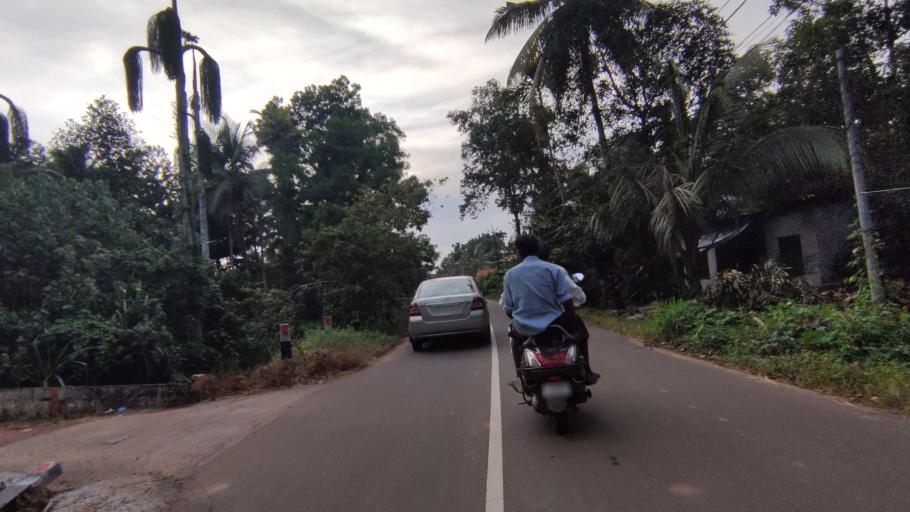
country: IN
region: Kerala
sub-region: Kottayam
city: Kottayam
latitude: 9.6371
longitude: 76.4938
